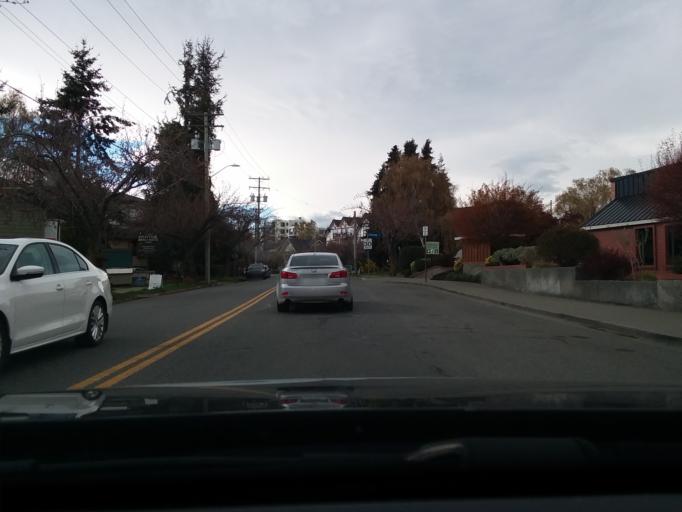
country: CA
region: British Columbia
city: Victoria
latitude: 48.4155
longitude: -123.3492
